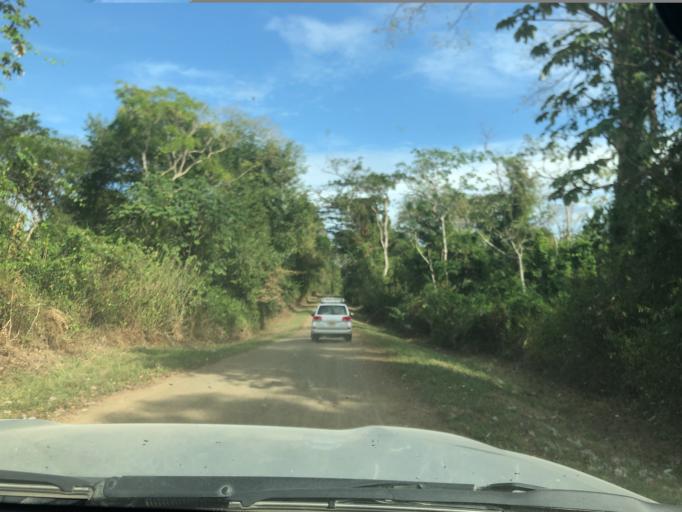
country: NI
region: Rivas
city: Cardenas
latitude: 11.1248
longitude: -85.2919
